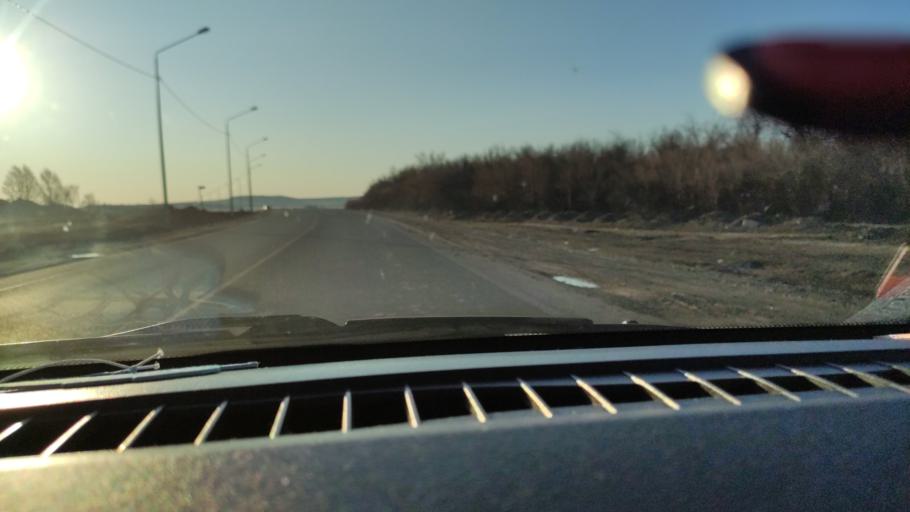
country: RU
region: Saratov
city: Sennoy
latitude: 52.1589
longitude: 47.0630
